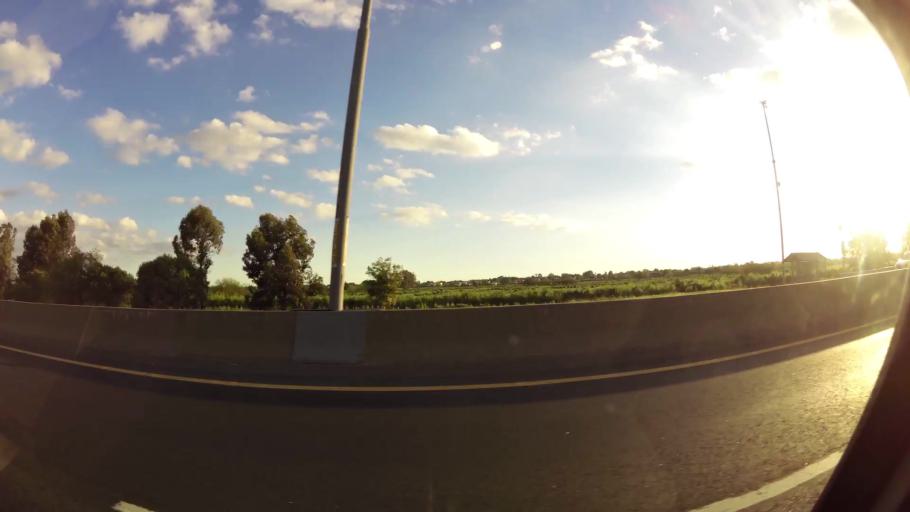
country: AR
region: Buenos Aires
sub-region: Partido de La Plata
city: La Plata
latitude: -34.8687
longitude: -57.9950
